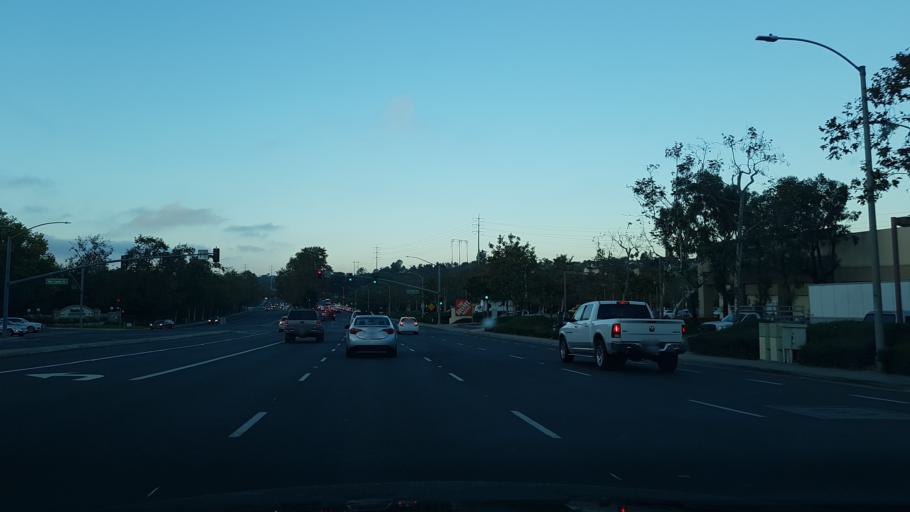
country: US
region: California
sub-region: San Diego County
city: Encinitas
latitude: 33.0641
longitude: -117.2624
